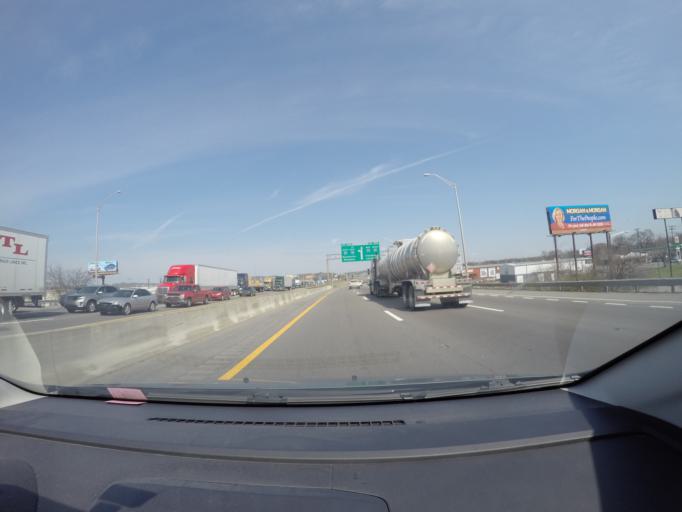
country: US
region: Tennessee
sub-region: Davidson County
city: Nashville
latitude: 36.1826
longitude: -86.7749
